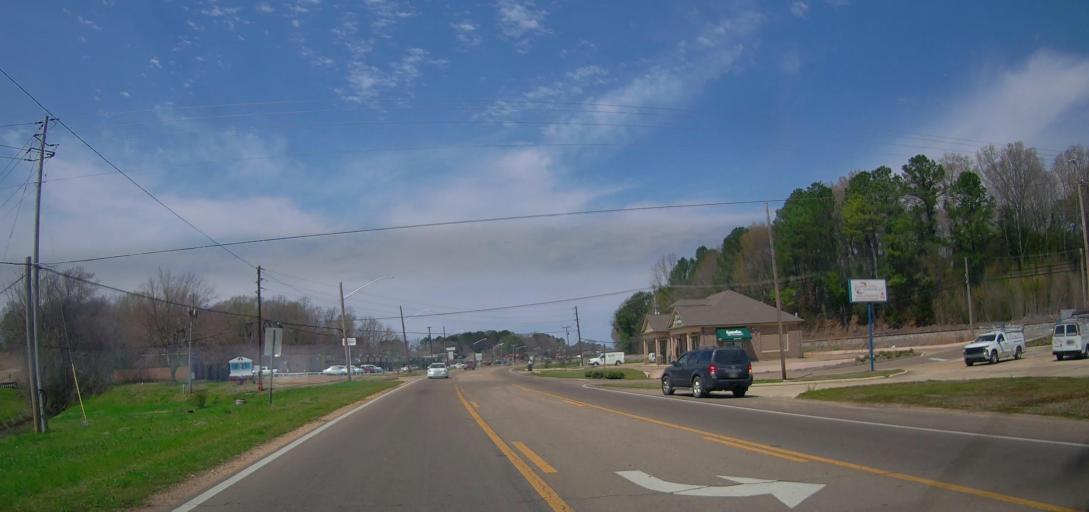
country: US
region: Mississippi
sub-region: Union County
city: New Albany
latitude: 34.4969
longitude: -89.0209
